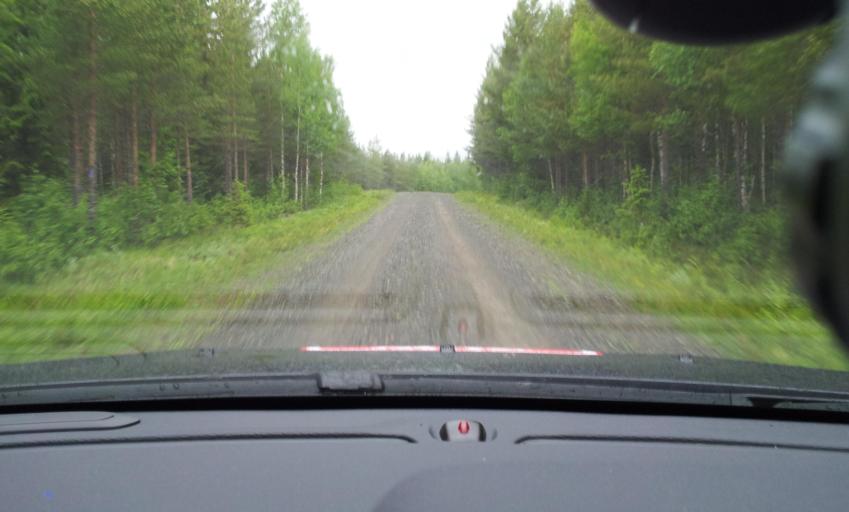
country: SE
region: Jaemtland
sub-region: Are Kommun
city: Are
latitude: 63.1875
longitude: 13.2025
